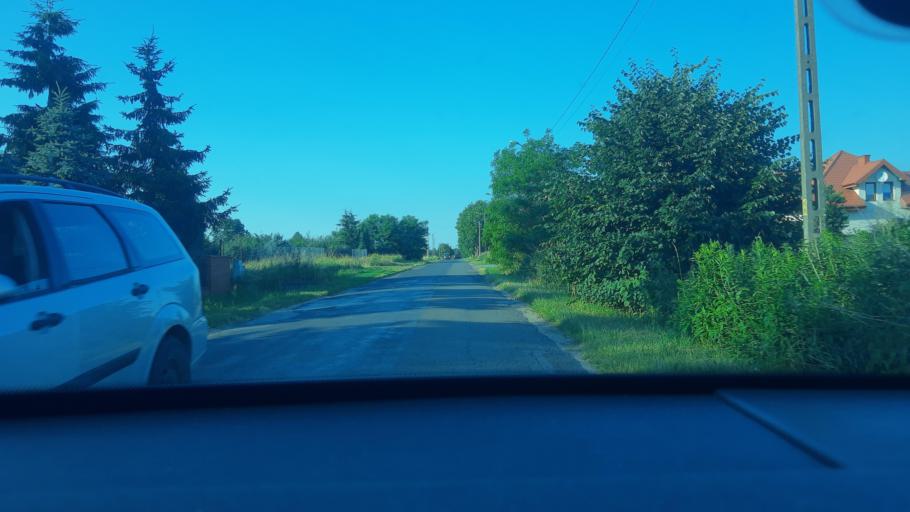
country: PL
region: Lodz Voivodeship
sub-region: Powiat sieradzki
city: Sieradz
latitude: 51.5507
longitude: 18.7590
